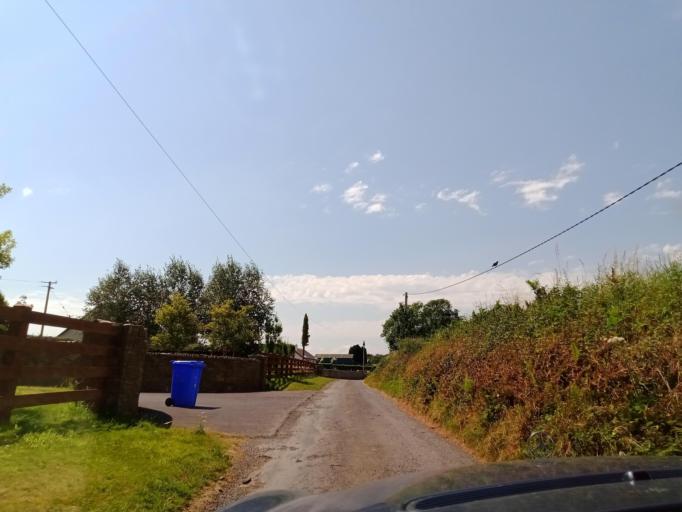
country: IE
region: Leinster
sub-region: Kilkenny
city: Mooncoin
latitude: 52.2752
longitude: -7.2367
